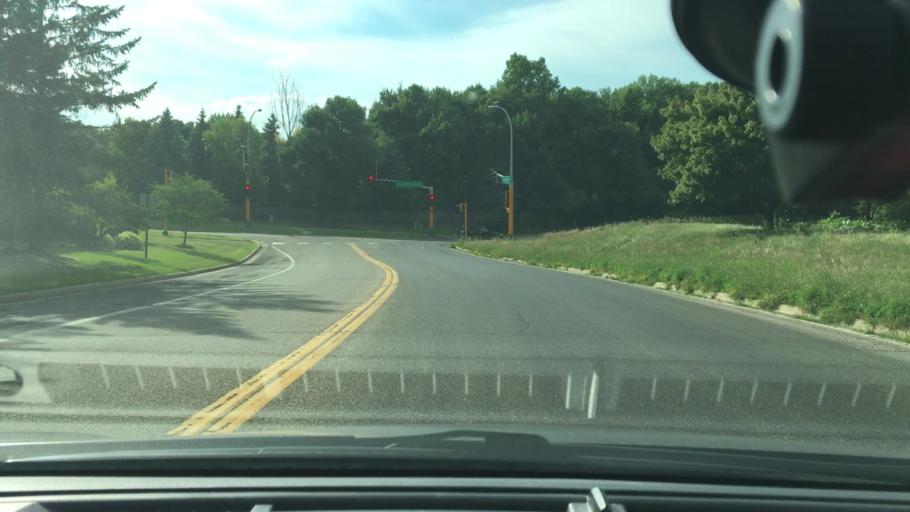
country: US
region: Minnesota
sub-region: Hennepin County
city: Plymouth
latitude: 45.0169
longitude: -93.4413
